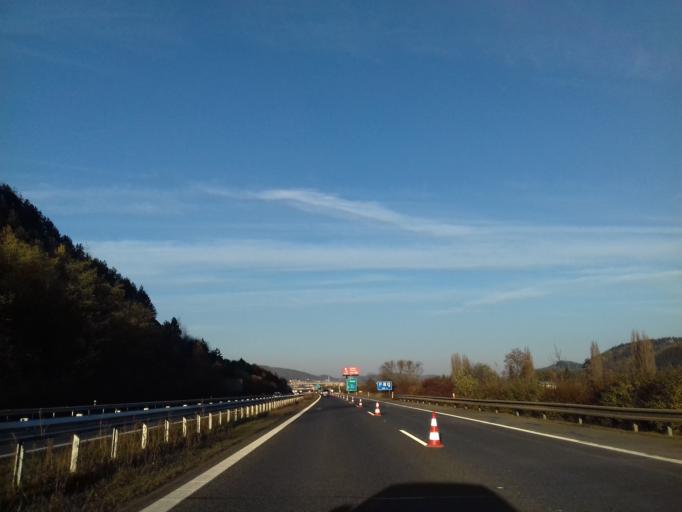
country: CZ
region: Central Bohemia
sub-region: Okres Beroun
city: Kraluv Dvur
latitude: 49.9257
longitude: 14.0111
